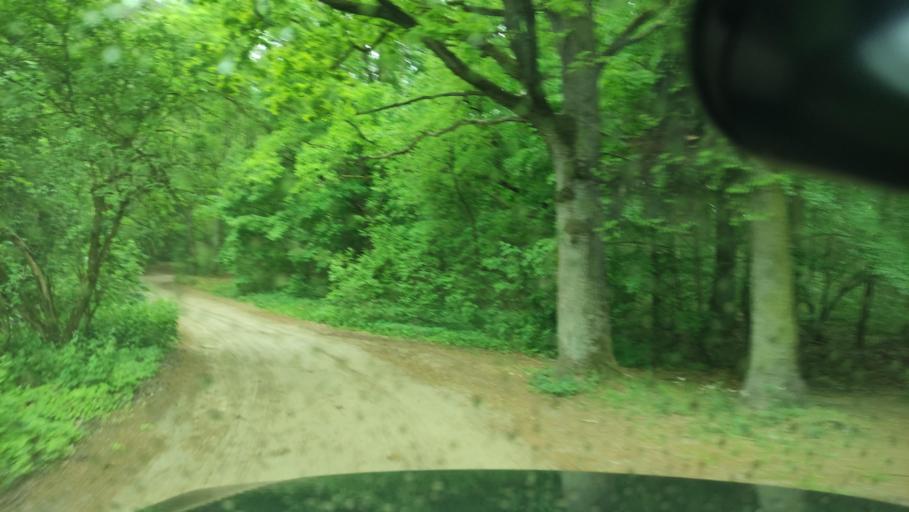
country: PL
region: Warmian-Masurian Voivodeship
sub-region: Powiat olsztynski
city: Olsztyn
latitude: 53.7607
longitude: 20.5221
